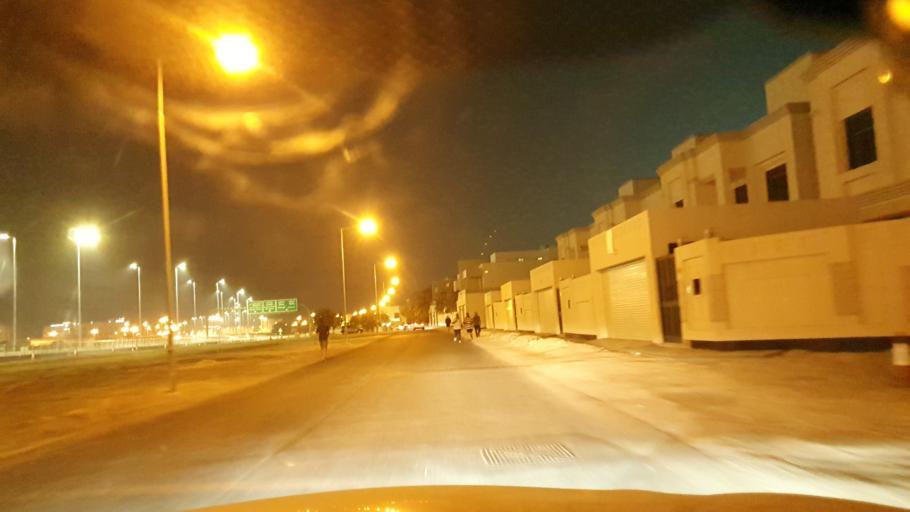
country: BH
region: Northern
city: Madinat `Isa
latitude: 26.1575
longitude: 50.5561
